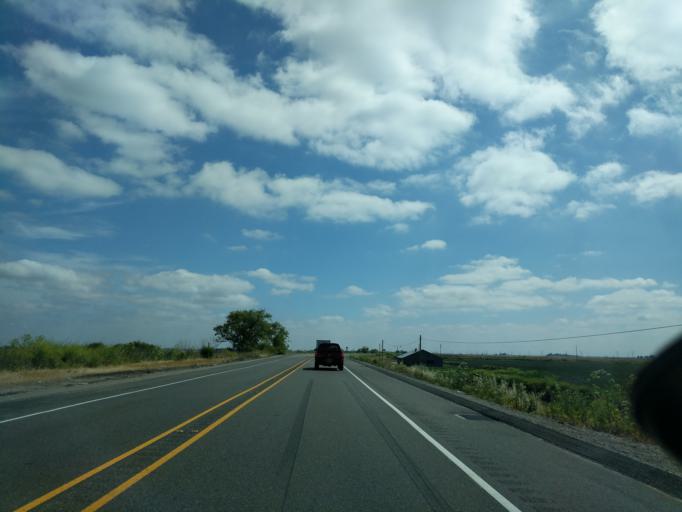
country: US
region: California
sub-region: Contra Costa County
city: Discovery Bay
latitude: 37.8997
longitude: -121.4717
